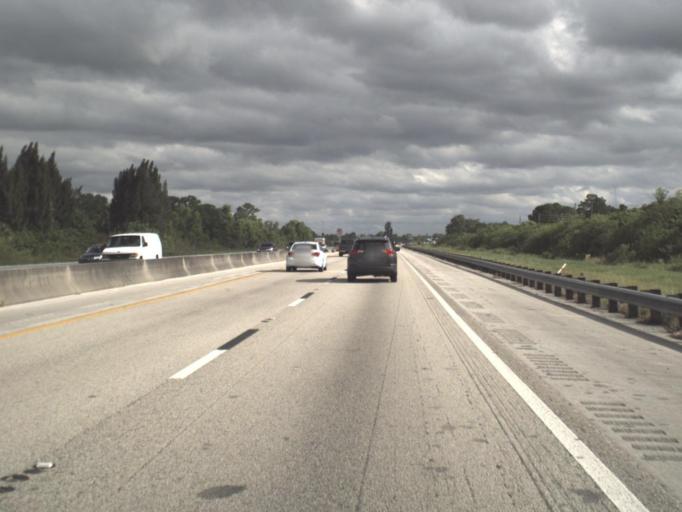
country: US
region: Florida
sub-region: Martin County
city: Palm City
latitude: 27.1045
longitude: -80.2649
